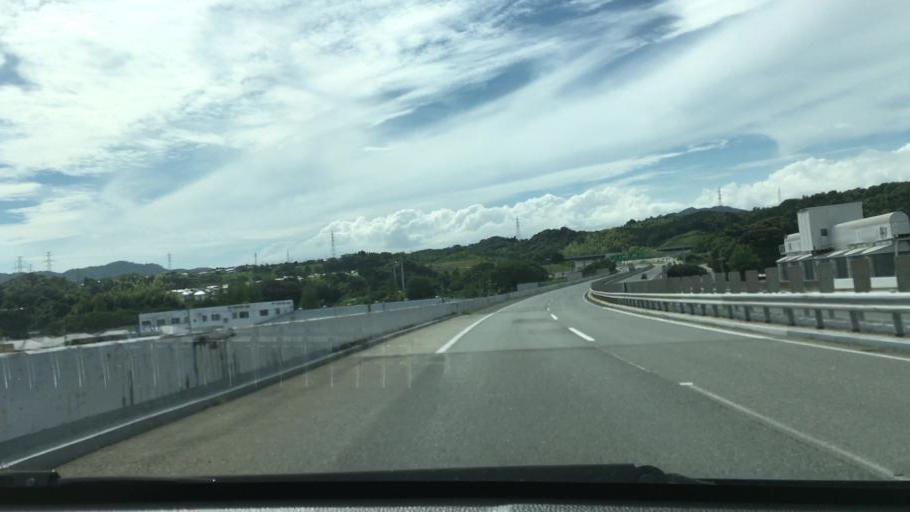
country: JP
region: Yamaguchi
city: Ogori-shimogo
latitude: 34.1231
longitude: 131.4120
